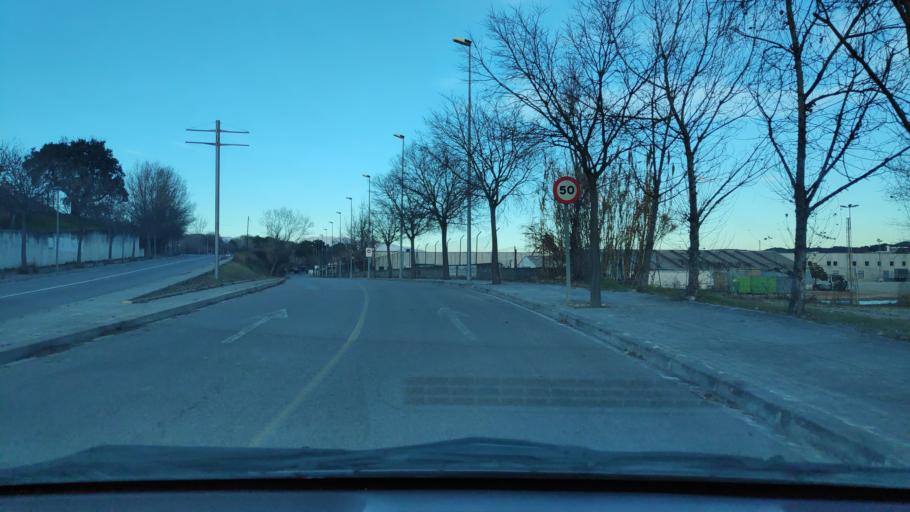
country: ES
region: Catalonia
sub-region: Provincia de Barcelona
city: Montmelo
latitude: 41.5596
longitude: 2.2558
